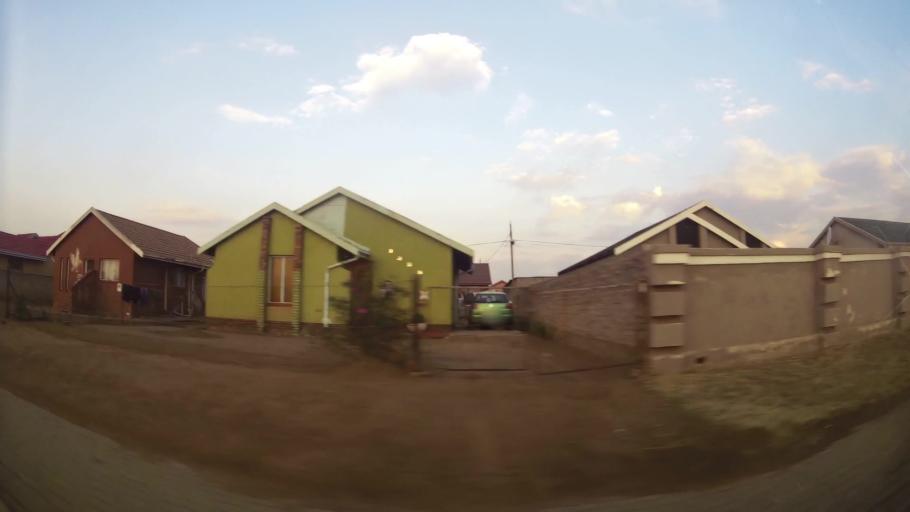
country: ZA
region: Gauteng
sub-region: City of Johannesburg Metropolitan Municipality
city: Orange Farm
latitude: -26.5445
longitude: 27.8852
